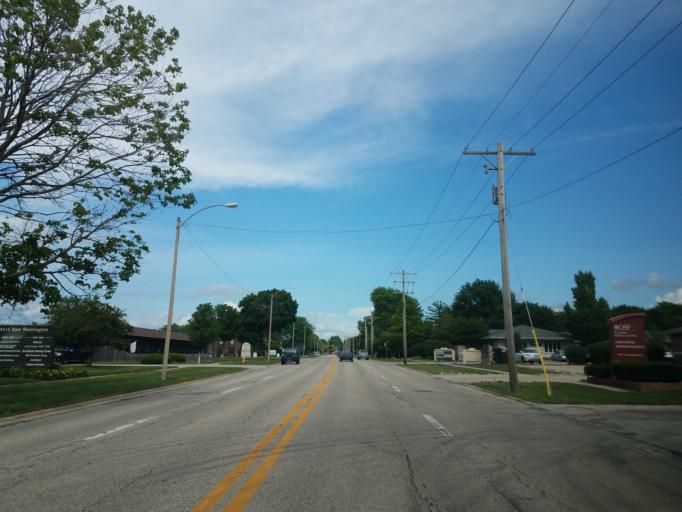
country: US
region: Illinois
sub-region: McLean County
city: Bloomington
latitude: 40.4800
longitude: -88.9483
